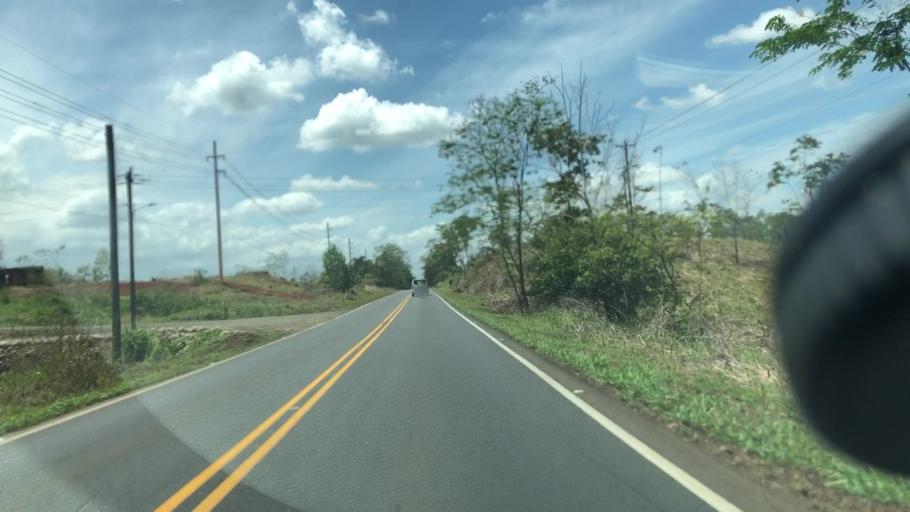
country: CR
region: Alajuela
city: Pital
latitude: 10.4576
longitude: -84.3980
